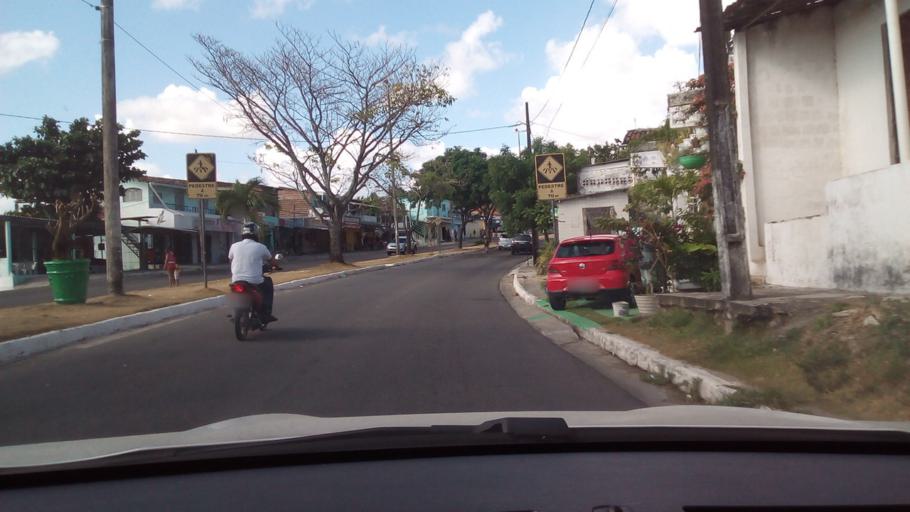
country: BR
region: Paraiba
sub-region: Joao Pessoa
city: Joao Pessoa
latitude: -7.1290
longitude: -34.8542
